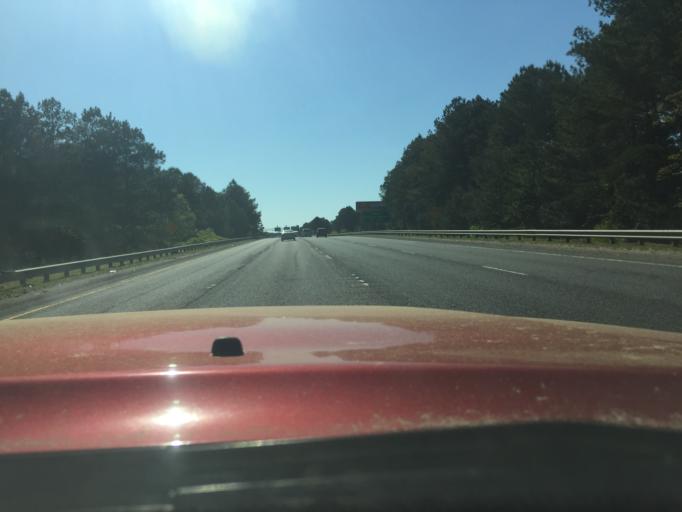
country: US
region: South Carolina
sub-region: Lexington County
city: Cayce
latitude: 33.9299
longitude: -81.0531
